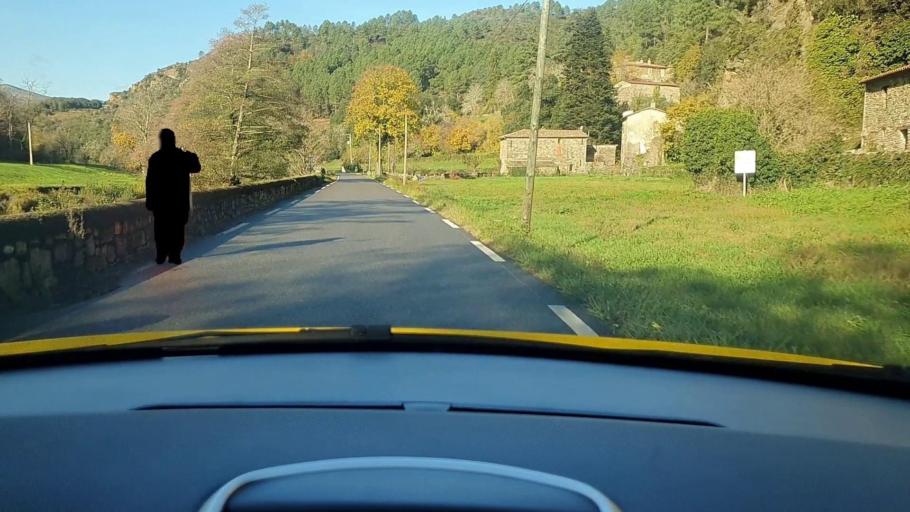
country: FR
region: Languedoc-Roussillon
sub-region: Departement du Gard
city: Valleraugue
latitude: 44.1369
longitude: 3.7518
